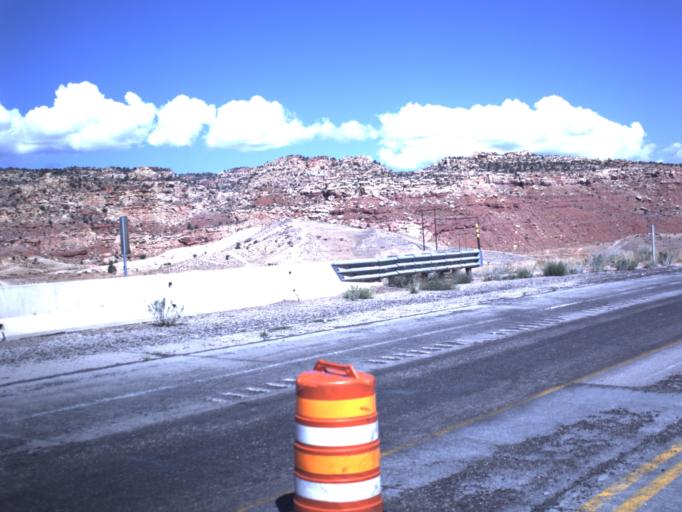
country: US
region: Utah
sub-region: Sevier County
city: Richfield
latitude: 38.7627
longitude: -112.1048
